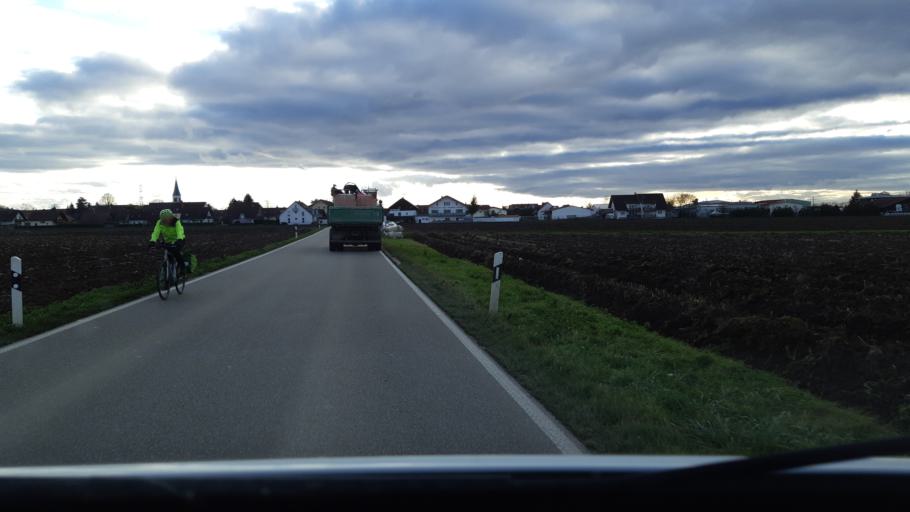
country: DE
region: Baden-Wuerttemberg
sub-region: Freiburg Region
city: Eschbach
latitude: 47.8959
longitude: 7.6564
